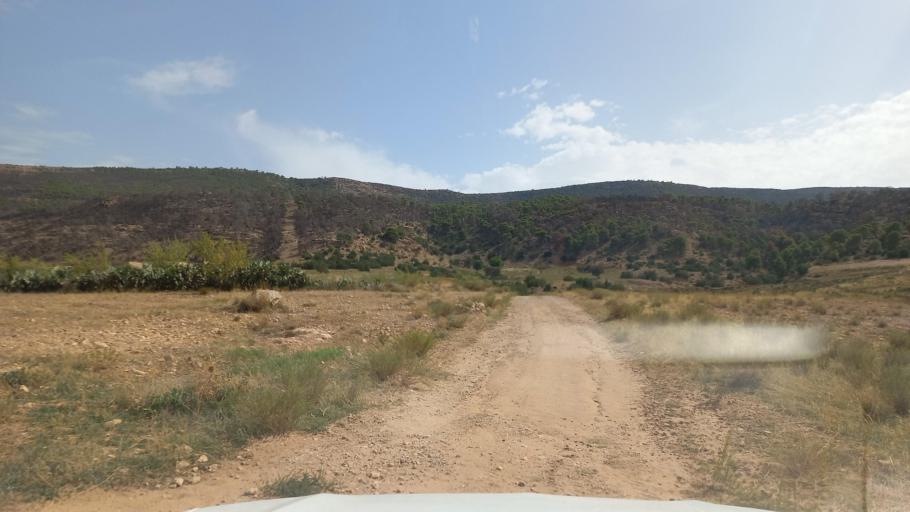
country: TN
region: Al Qasrayn
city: Kasserine
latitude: 35.3555
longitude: 8.8896
